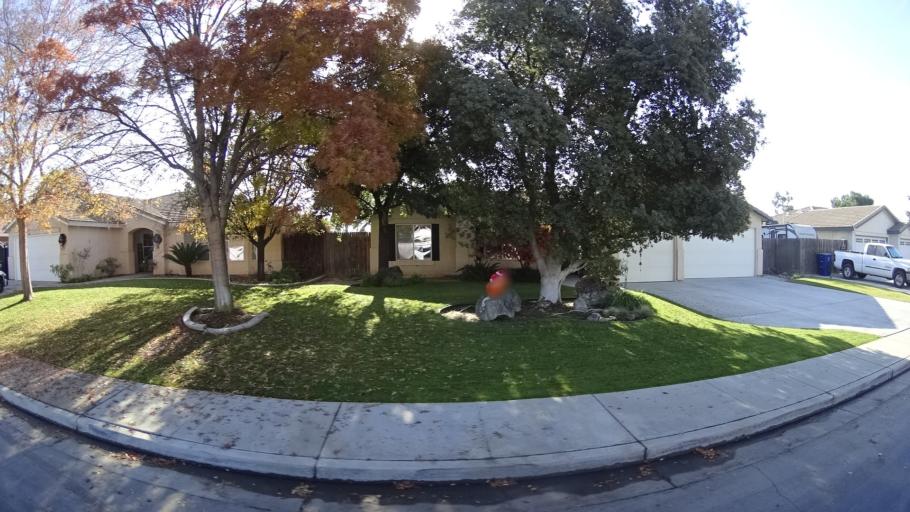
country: US
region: California
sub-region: Kern County
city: Oildale
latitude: 35.4025
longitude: -119.0642
